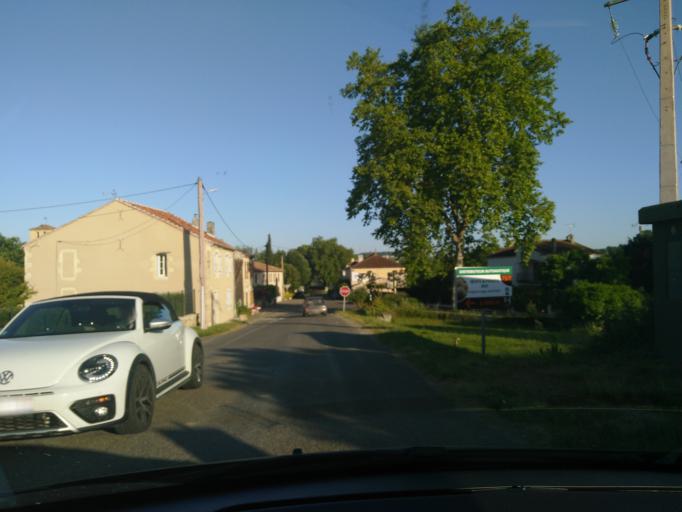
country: FR
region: Midi-Pyrenees
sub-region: Departement du Gers
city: Gondrin
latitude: 43.9041
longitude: 0.2999
